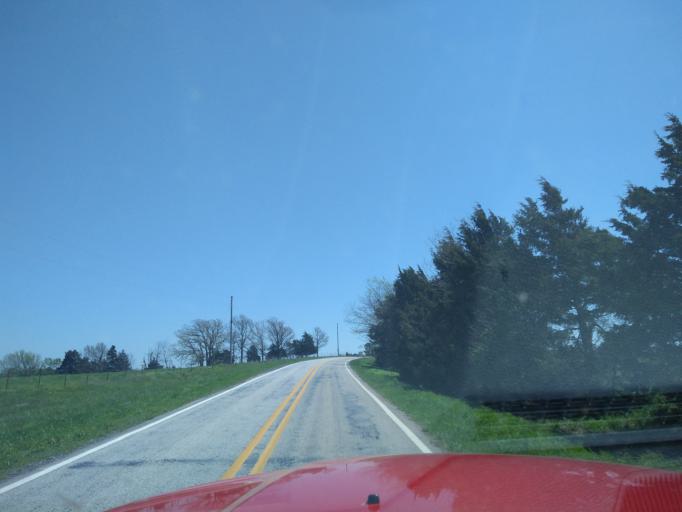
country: US
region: Arkansas
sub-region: Washington County
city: West Fork
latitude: 35.9007
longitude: -94.2098
